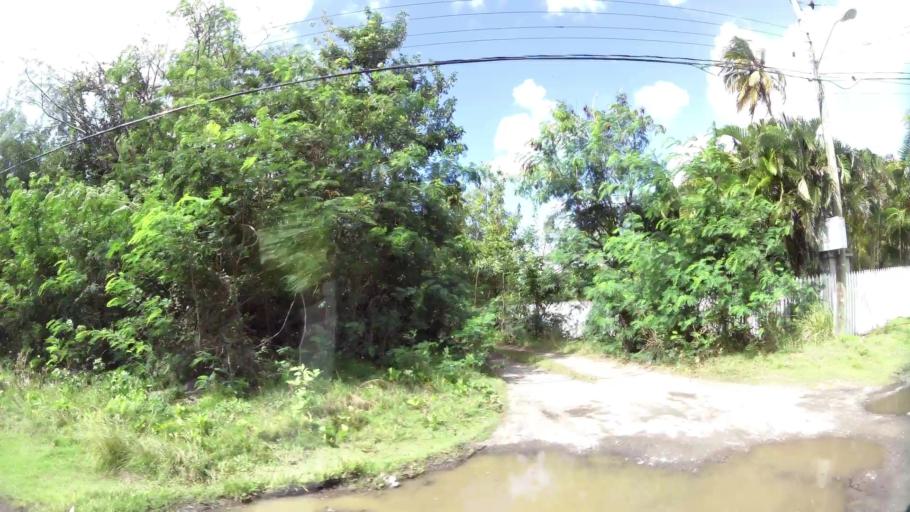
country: KN
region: Saint Thomas Lowland
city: Cotton Ground
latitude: 17.1765
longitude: -62.6243
